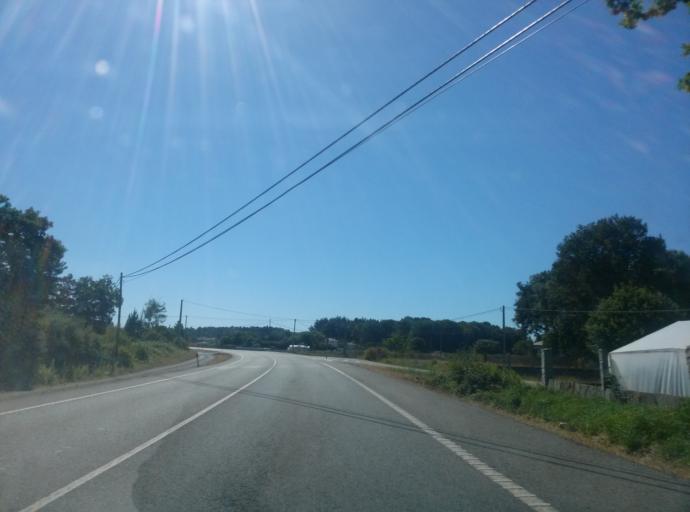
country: ES
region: Galicia
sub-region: Provincia de Lugo
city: Mos
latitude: 43.1227
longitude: -7.5590
